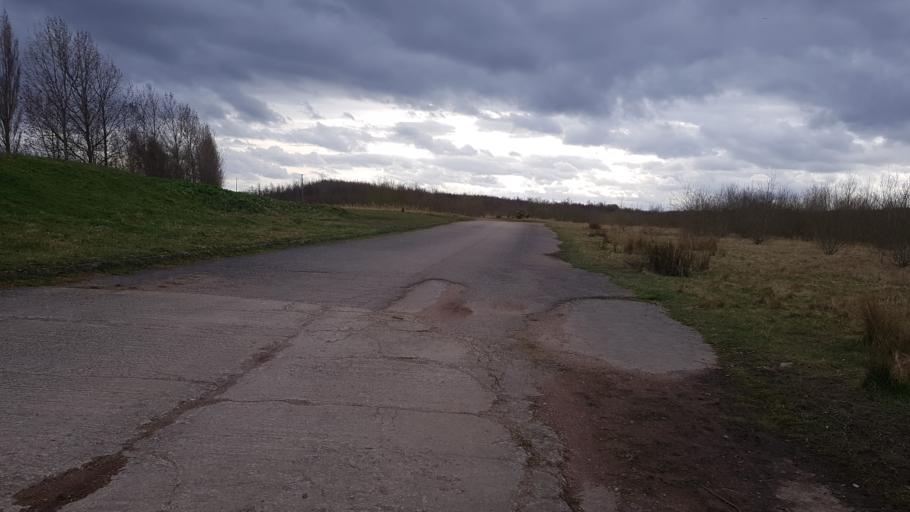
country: GB
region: England
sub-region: City and Borough of Leeds
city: Swillington
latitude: 53.7479
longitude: -1.3947
